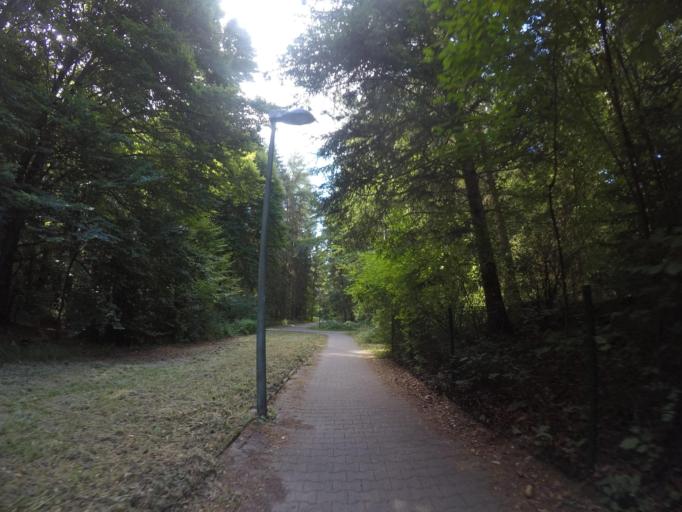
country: DE
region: Baden-Wuerttemberg
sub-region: Tuebingen Region
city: Staig
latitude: 48.3432
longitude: 9.9724
